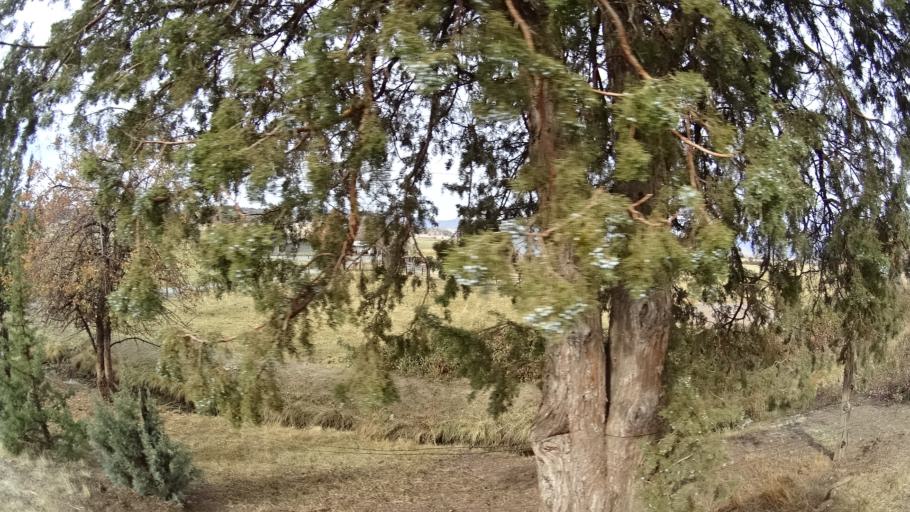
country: US
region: California
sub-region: Siskiyou County
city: Montague
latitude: 41.6966
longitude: -122.5539
